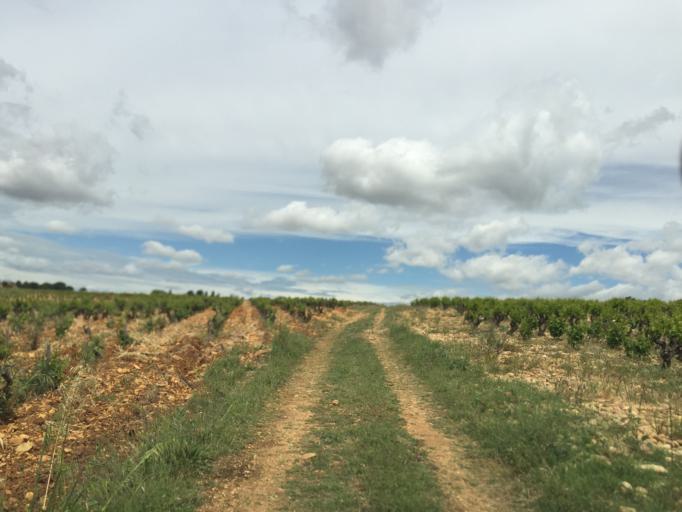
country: FR
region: Provence-Alpes-Cote d'Azur
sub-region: Departement du Vaucluse
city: Bedarrides
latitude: 44.0430
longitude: 4.8733
